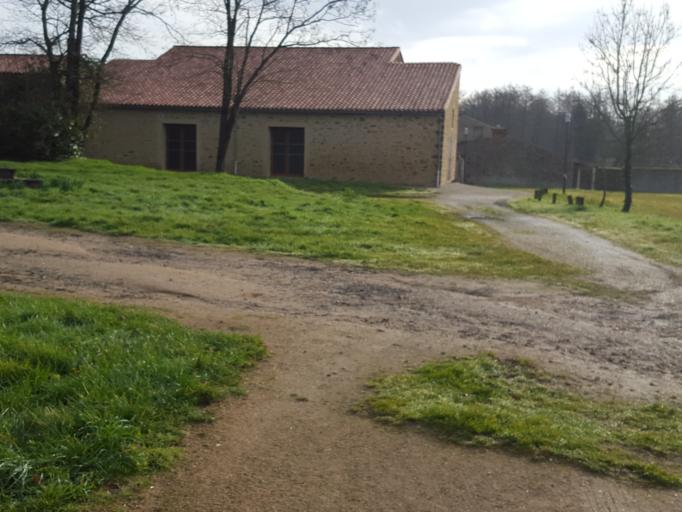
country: FR
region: Pays de la Loire
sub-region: Departement de la Vendee
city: Mouilleron-le-Captif
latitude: 46.7115
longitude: -1.4390
